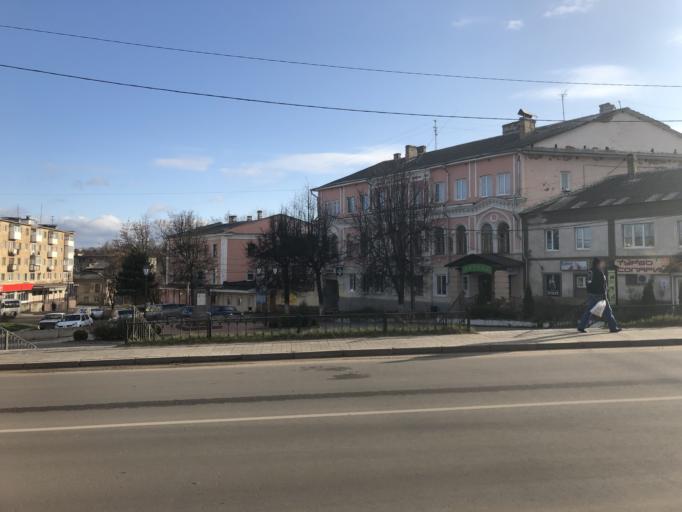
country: RU
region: Tverskaya
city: Rzhev
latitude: 56.2582
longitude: 34.3284
